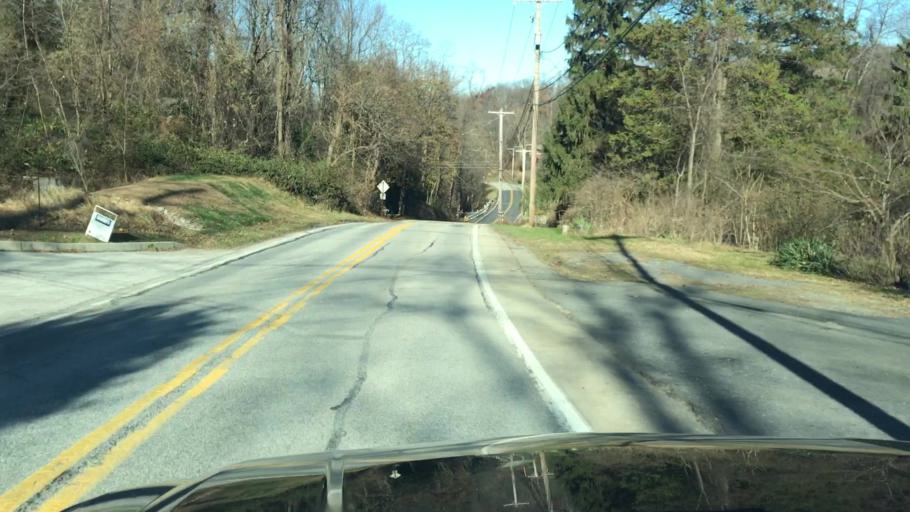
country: US
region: Pennsylvania
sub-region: Cumberland County
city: Lower Allen
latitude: 40.1826
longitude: -76.8828
